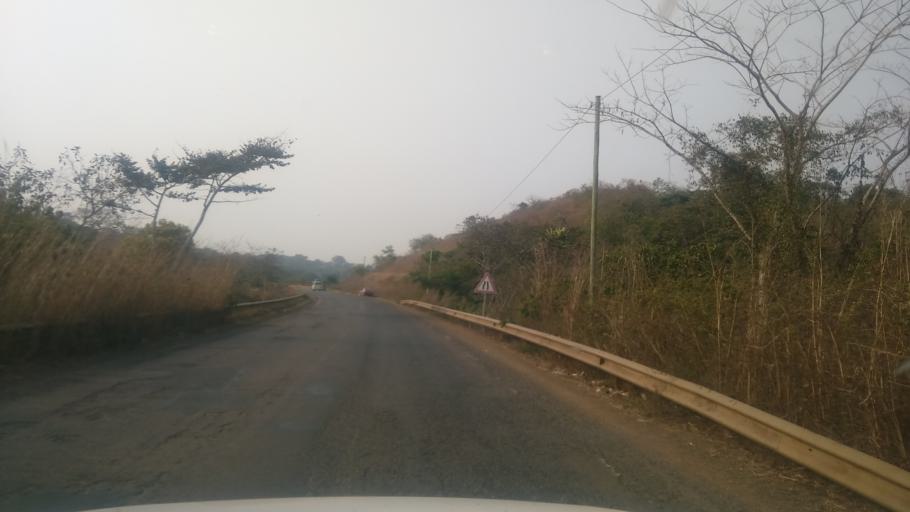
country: CM
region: West
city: Tonga
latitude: 5.0532
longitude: 10.6988
